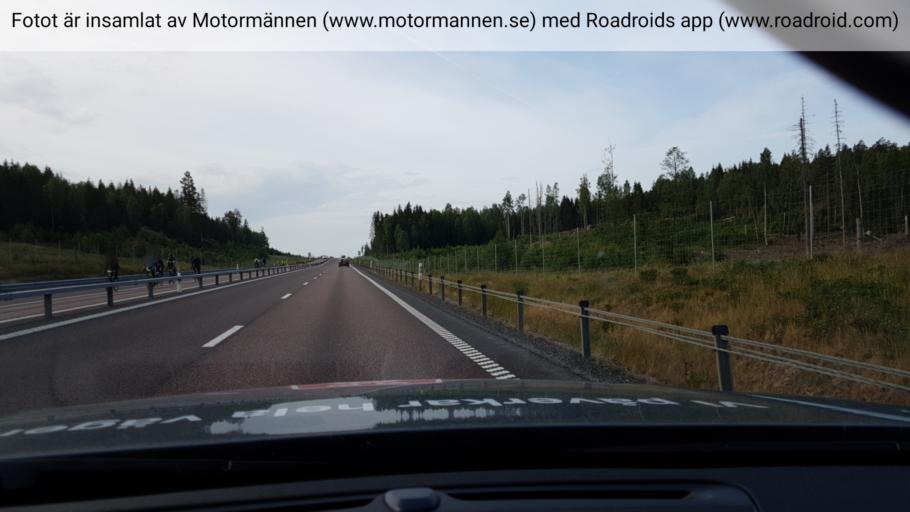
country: SE
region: OErebro
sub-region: Askersunds Kommun
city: Askersund
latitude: 58.8439
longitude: 14.9069
